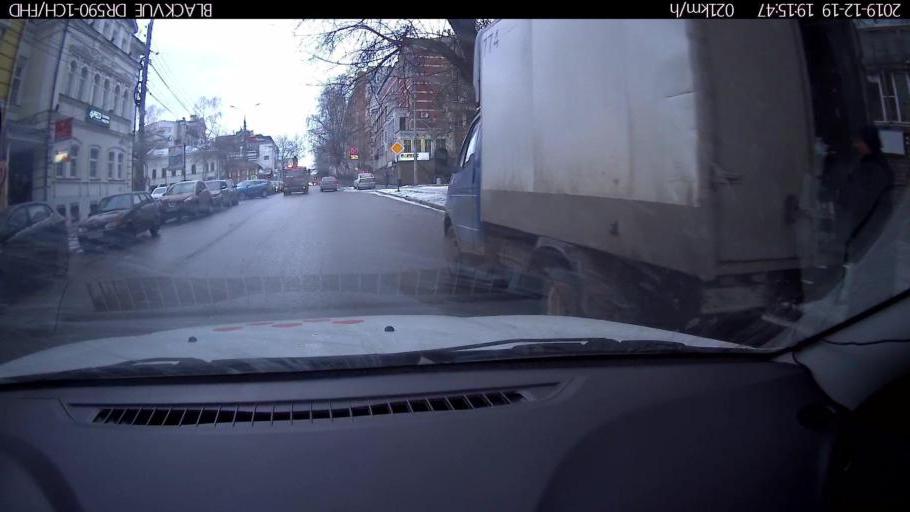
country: RU
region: Nizjnij Novgorod
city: Nizhniy Novgorod
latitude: 56.3199
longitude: 44.0095
